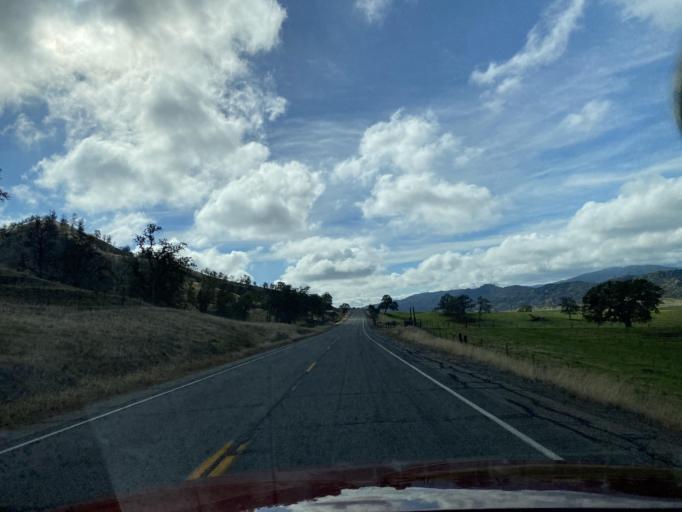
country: US
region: California
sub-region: Glenn County
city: Willows
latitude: 39.5633
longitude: -122.5415
